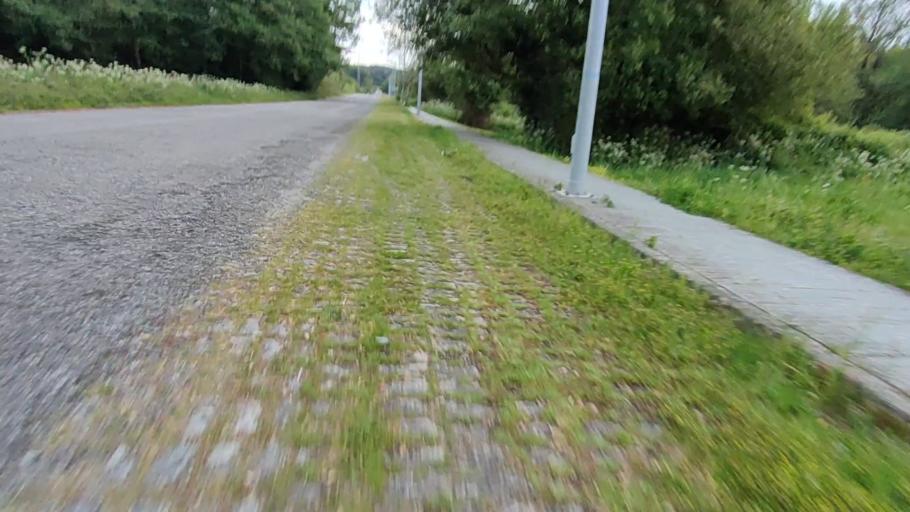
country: ES
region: Galicia
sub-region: Provincia da Coruna
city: Boiro
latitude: 42.6127
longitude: -8.8683
